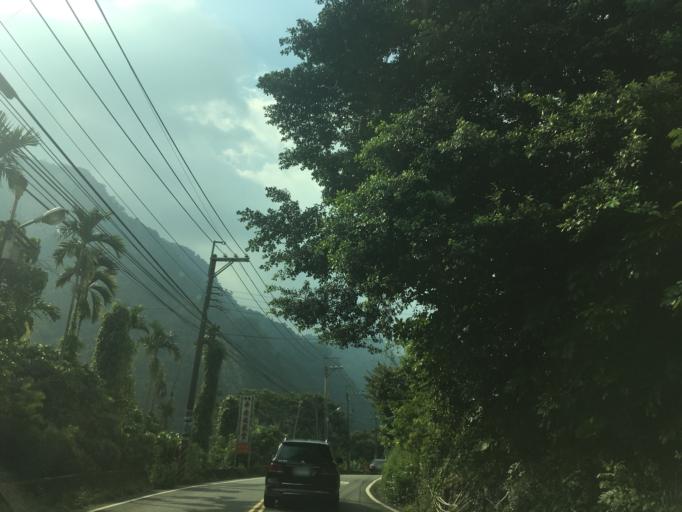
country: TW
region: Taiwan
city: Fengyuan
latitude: 24.3079
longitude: 120.9238
